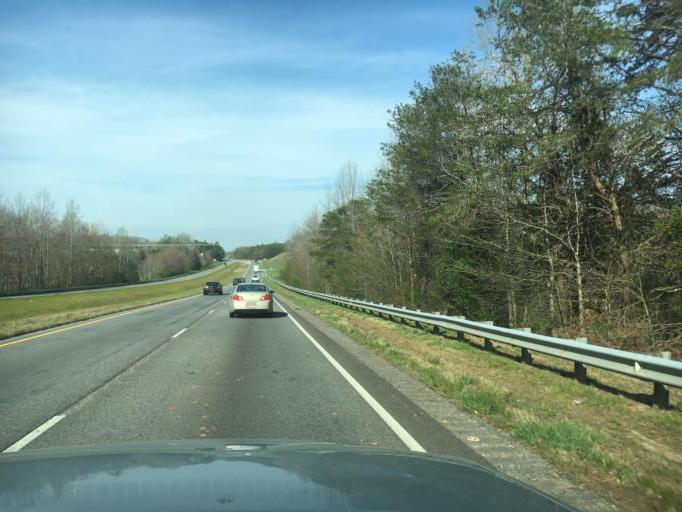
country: US
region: Georgia
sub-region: Habersham County
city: Raoul
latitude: 34.4713
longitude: -83.5959
